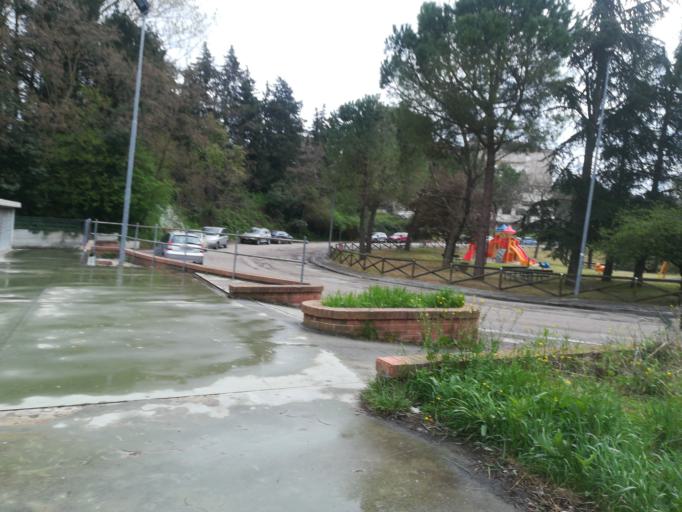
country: IT
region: The Marches
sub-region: Provincia di Macerata
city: Macerata
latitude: 43.2946
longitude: 13.4520
